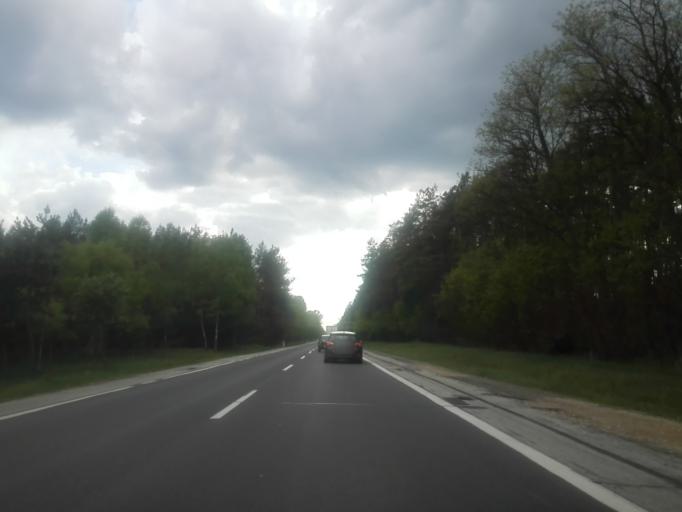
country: PL
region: Masovian Voivodeship
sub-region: Powiat ostrowski
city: Brok
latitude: 52.7670
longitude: 21.8185
